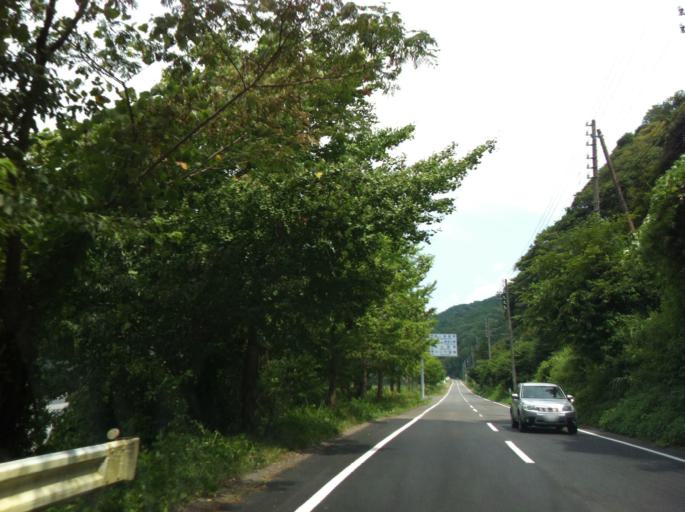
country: JP
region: Shizuoka
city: Shizuoka-shi
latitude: 35.1158
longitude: 138.3609
